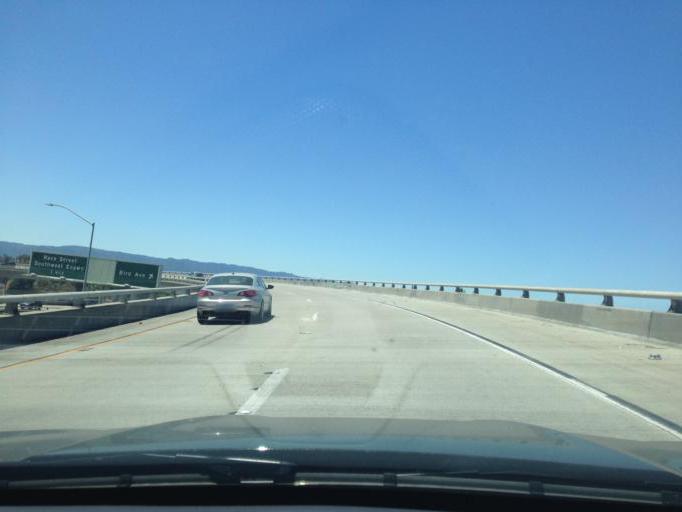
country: US
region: California
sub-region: Santa Clara County
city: San Jose
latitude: 37.3249
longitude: -121.8906
